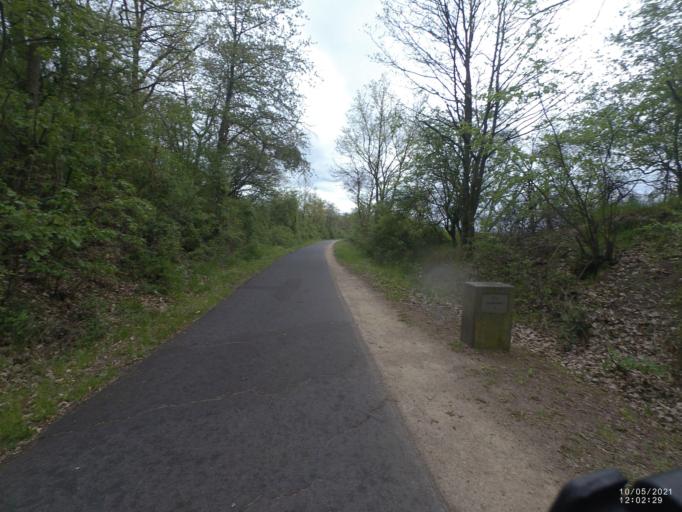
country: DE
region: Rheinland-Pfalz
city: Kerben
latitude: 50.3166
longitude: 7.3640
